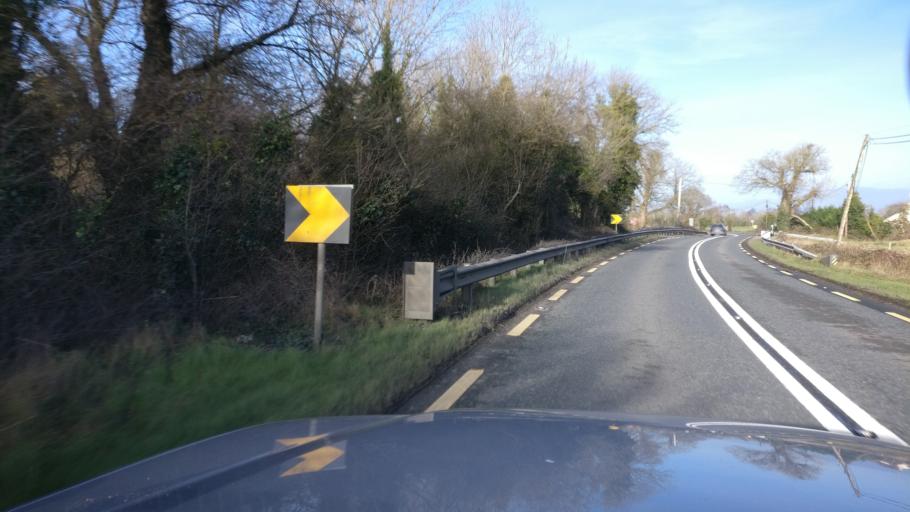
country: IE
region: Leinster
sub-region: Laois
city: Mountmellick
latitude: 53.1548
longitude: -7.3698
